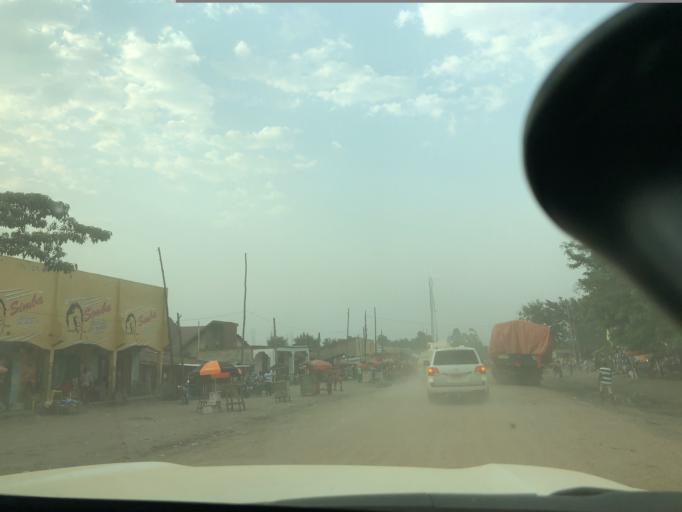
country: UG
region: Western Region
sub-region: Kasese District
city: Margherita
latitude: 0.3293
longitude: 29.6755
